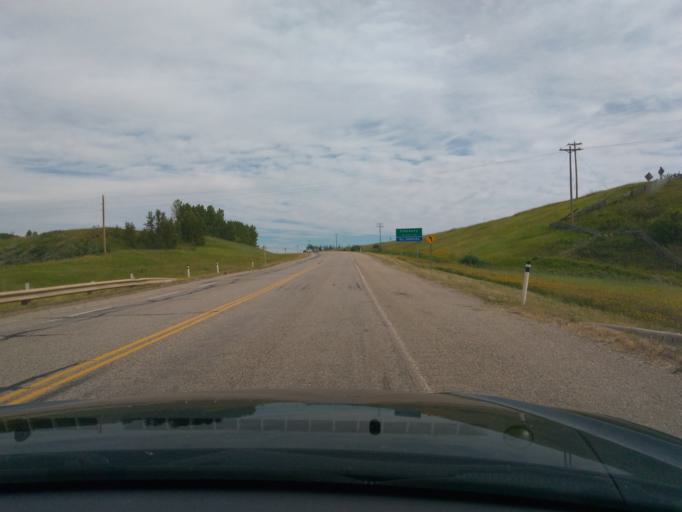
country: CA
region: Alberta
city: Didsbury
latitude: 51.6560
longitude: -114.0966
